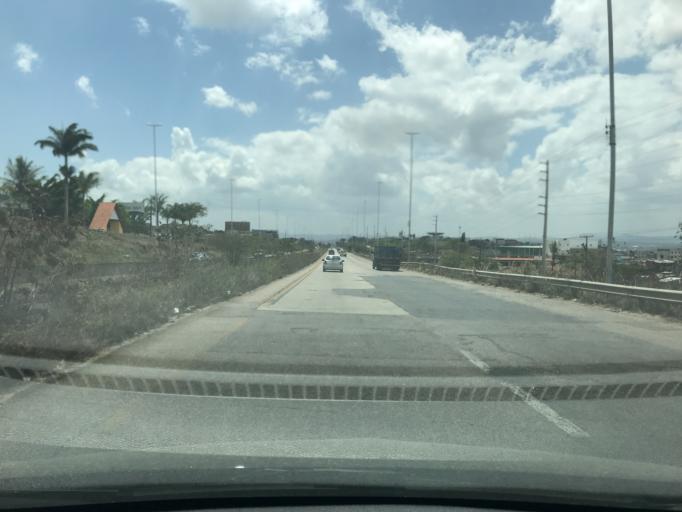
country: BR
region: Pernambuco
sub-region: Caruaru
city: Caruaru
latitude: -8.3047
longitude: -35.9696
